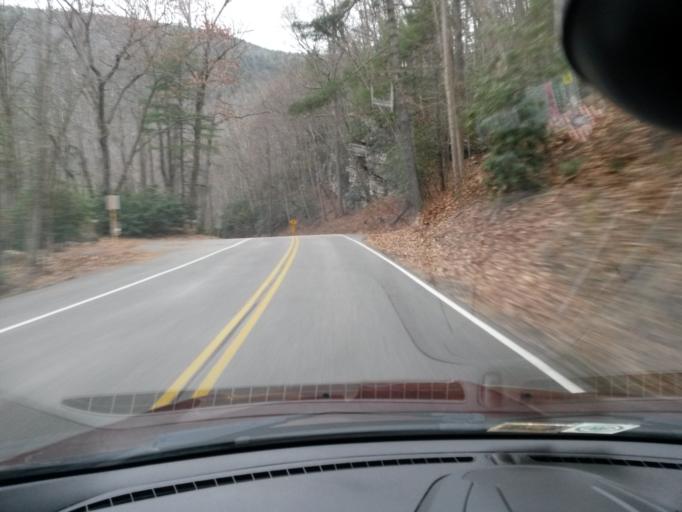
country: US
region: Virginia
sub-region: Rockbridge County
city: East Lexington
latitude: 37.9308
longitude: -79.4562
